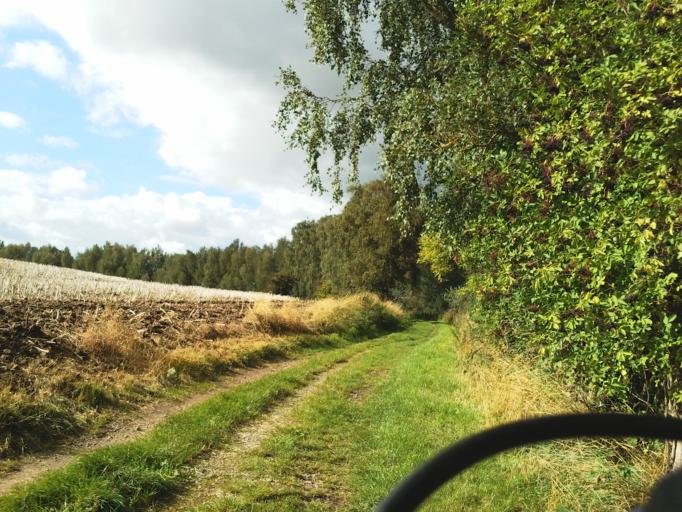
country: DE
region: Mecklenburg-Vorpommern
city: Dierkow-West
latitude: 54.1083
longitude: 12.1285
